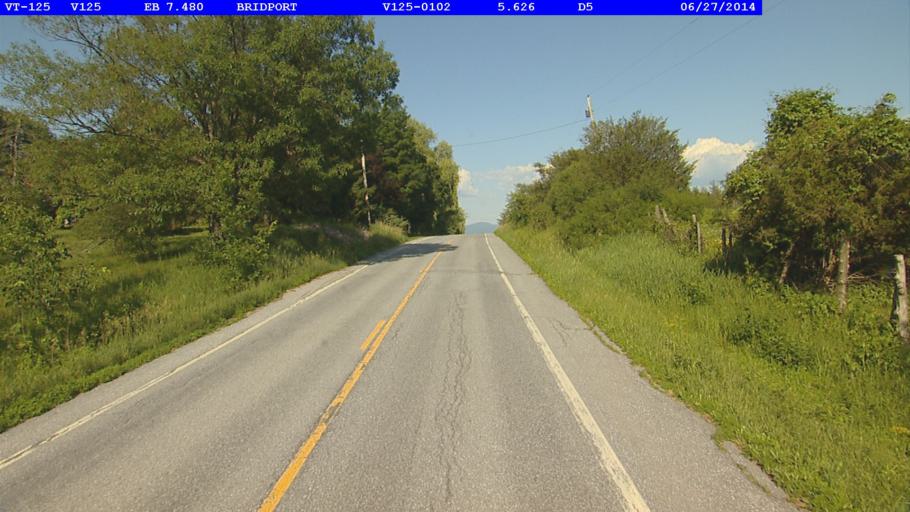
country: US
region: Vermont
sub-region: Addison County
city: Middlebury (village)
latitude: 43.9893
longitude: -73.3049
